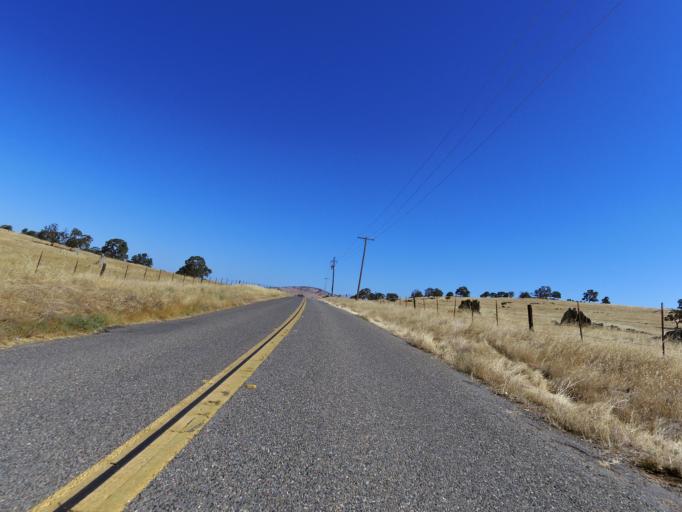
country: US
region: California
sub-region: Merced County
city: Planada
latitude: 37.5896
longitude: -120.3070
